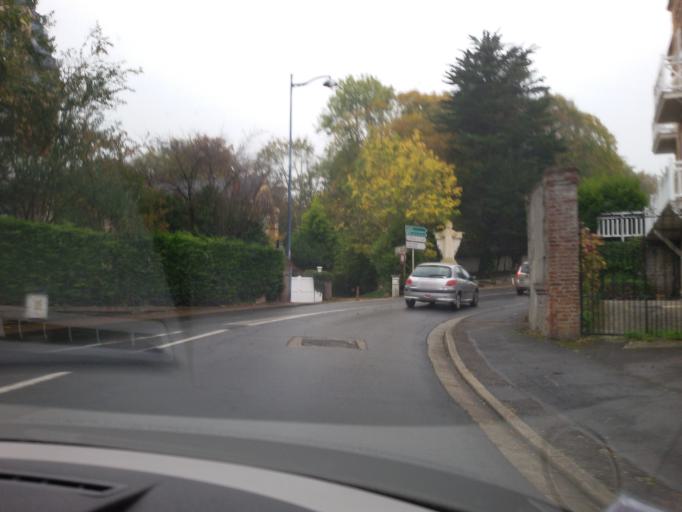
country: FR
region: Lower Normandy
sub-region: Departement du Calvados
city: Villers-sur-Mer
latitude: 49.3193
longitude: -0.0068
